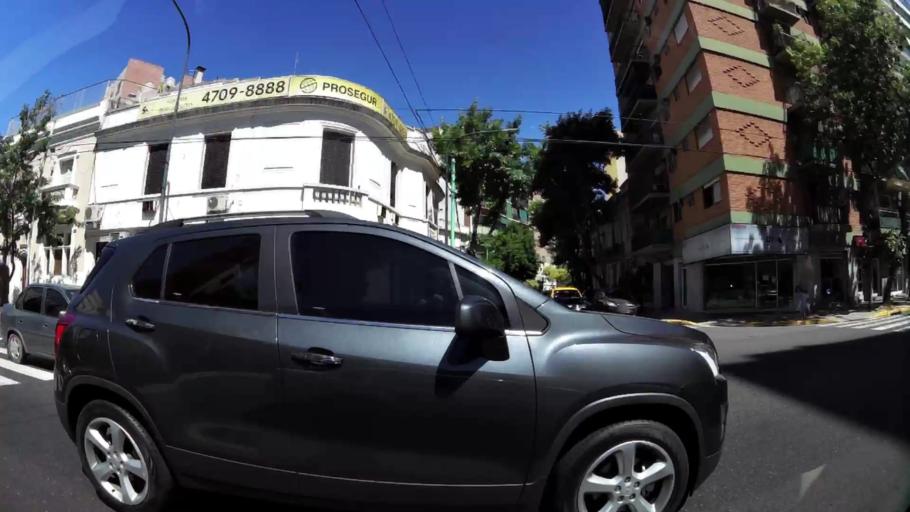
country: AR
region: Buenos Aires F.D.
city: Villa Santa Rita
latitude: -34.6238
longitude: -58.4451
